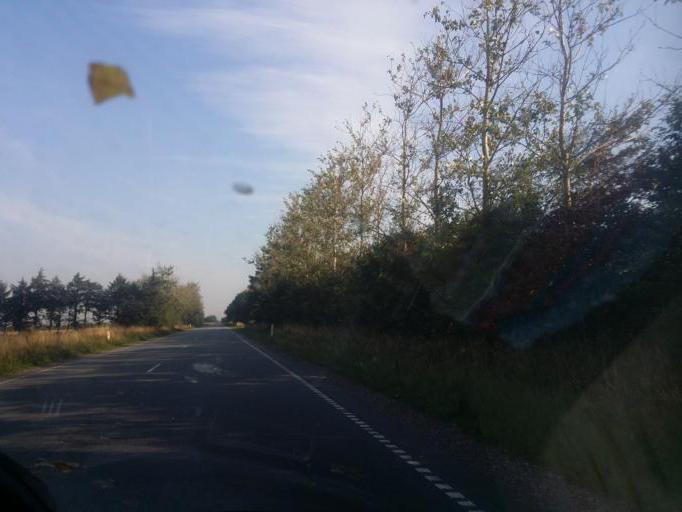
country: DK
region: South Denmark
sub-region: Tonder Kommune
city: Sherrebek
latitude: 55.0727
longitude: 8.8276
